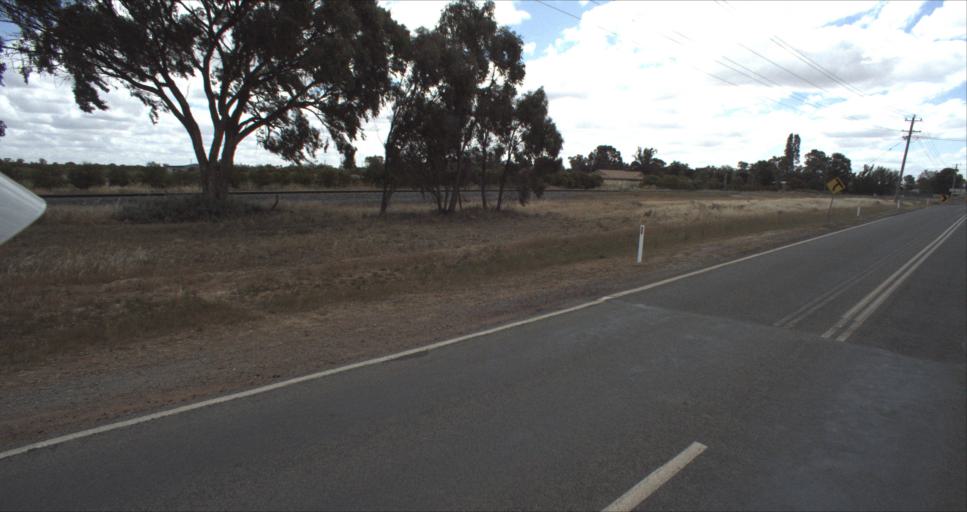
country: AU
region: New South Wales
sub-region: Leeton
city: Leeton
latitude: -34.5725
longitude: 146.3946
